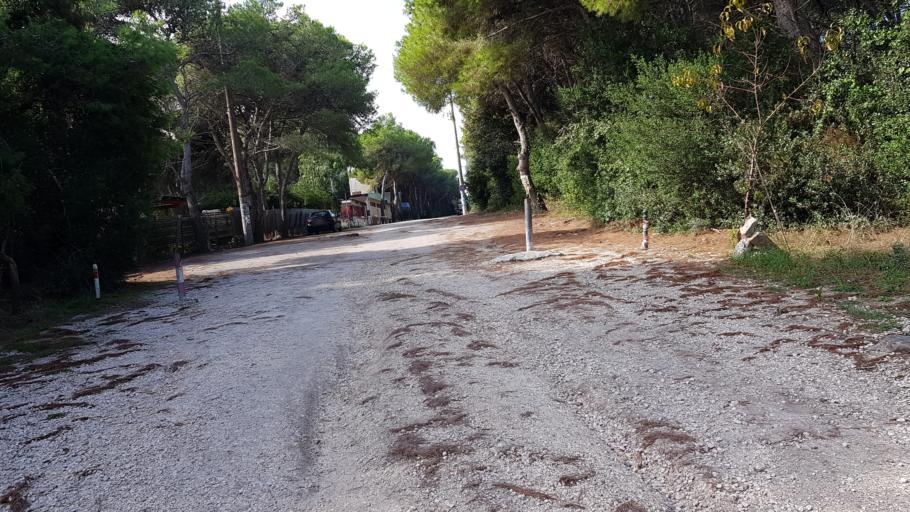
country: IT
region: Apulia
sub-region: Provincia di Lecce
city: Borgagne
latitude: 40.2331
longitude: 18.4588
